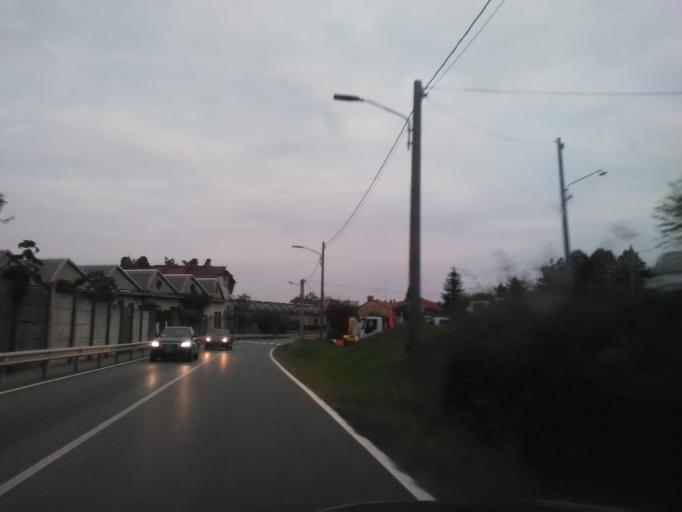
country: IT
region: Piedmont
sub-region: Provincia di Vercelli
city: Serravalle Sesia
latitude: 45.6852
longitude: 8.3076
